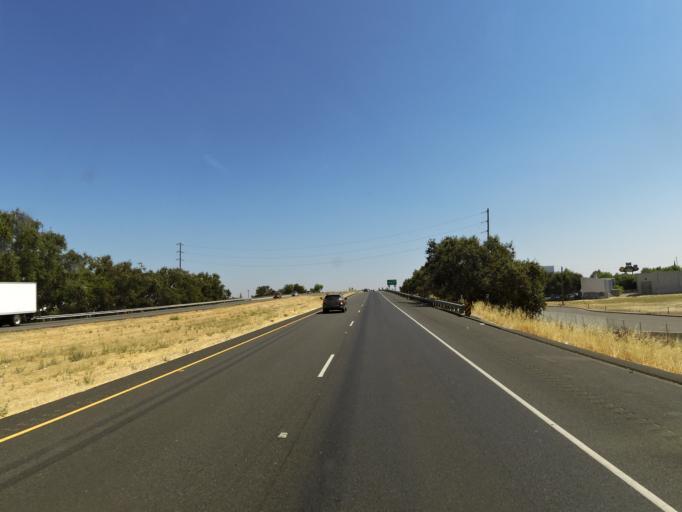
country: US
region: California
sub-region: Yolo County
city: Woodland
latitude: 38.6807
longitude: -121.7484
